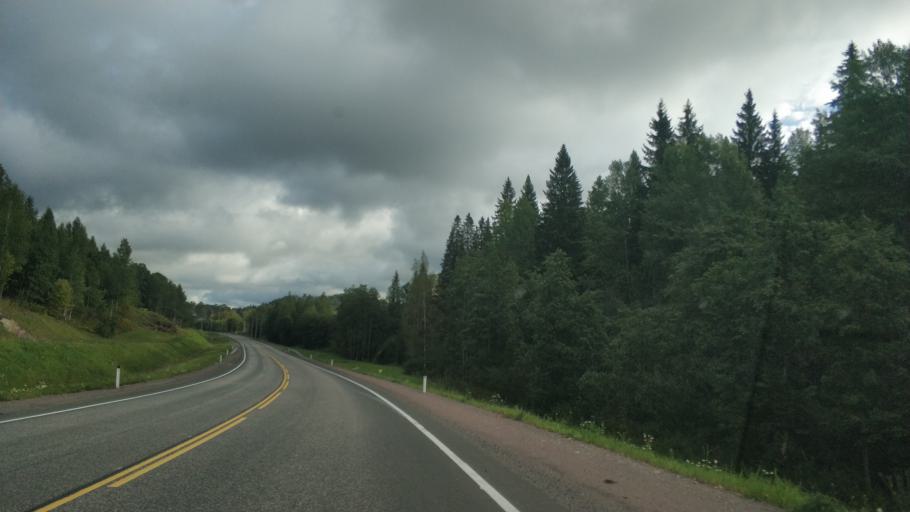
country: RU
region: Republic of Karelia
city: Khelyulya
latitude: 61.8128
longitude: 30.6273
